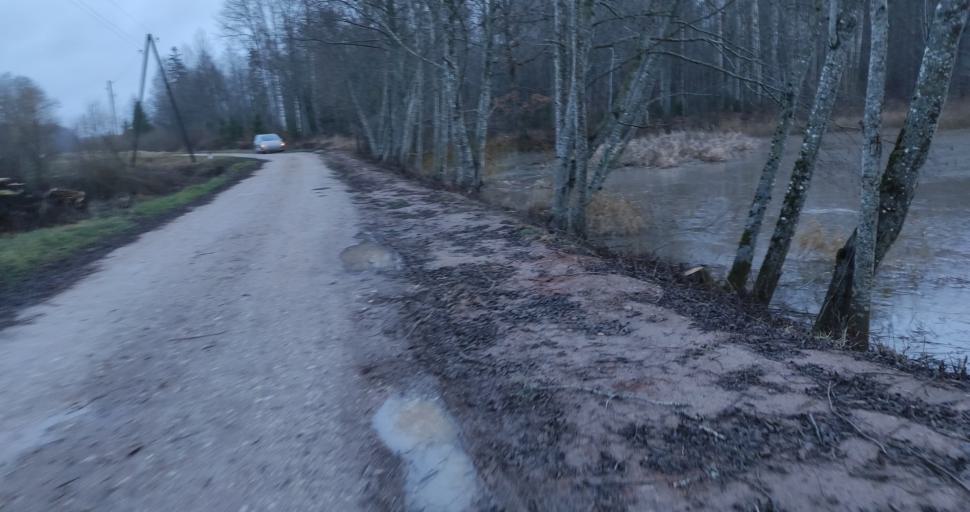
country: LV
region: Skrunda
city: Skrunda
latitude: 56.8704
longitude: 22.2424
